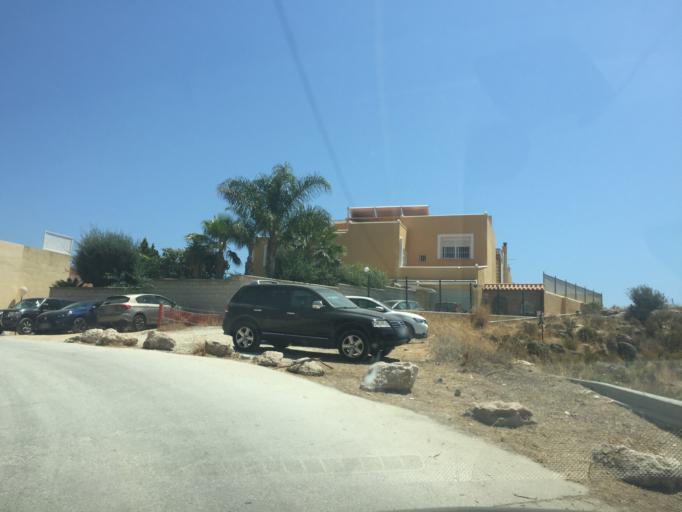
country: ES
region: Andalusia
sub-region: Provincia de Malaga
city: Nerja
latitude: 36.7641
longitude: -3.8745
